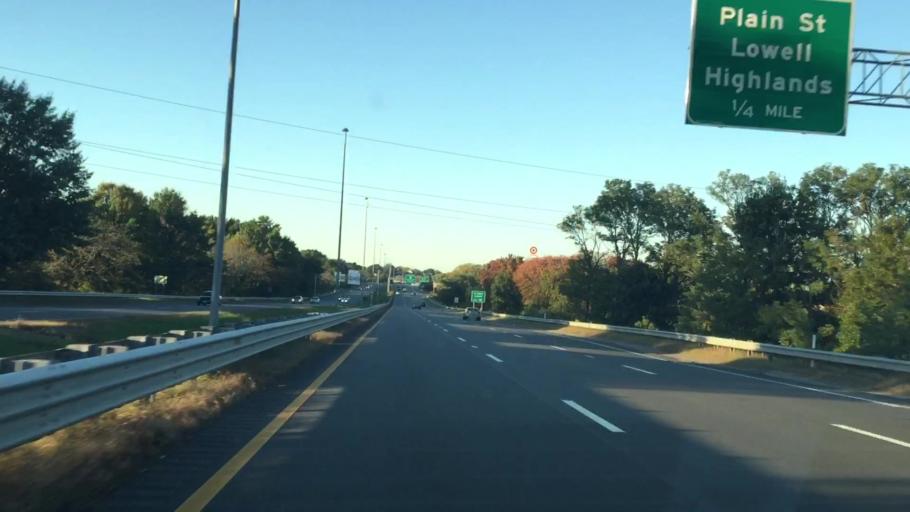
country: US
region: Massachusetts
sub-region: Middlesex County
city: Lowell
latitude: 42.6187
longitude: -71.3201
